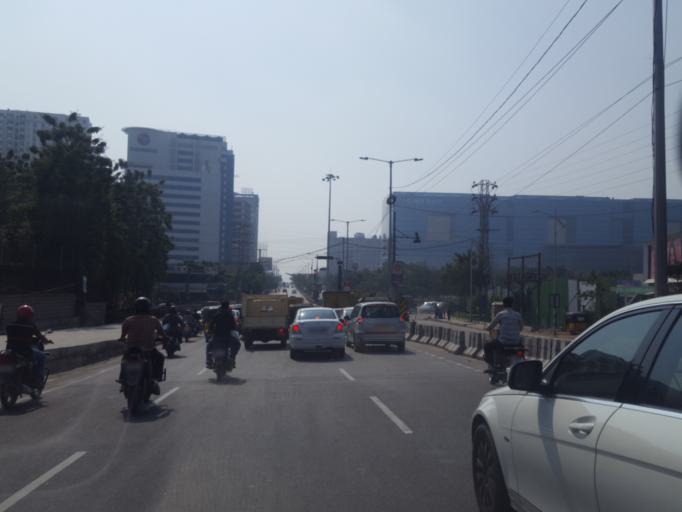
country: IN
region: Telangana
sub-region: Medak
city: Serilingampalle
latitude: 17.4267
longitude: 78.3412
